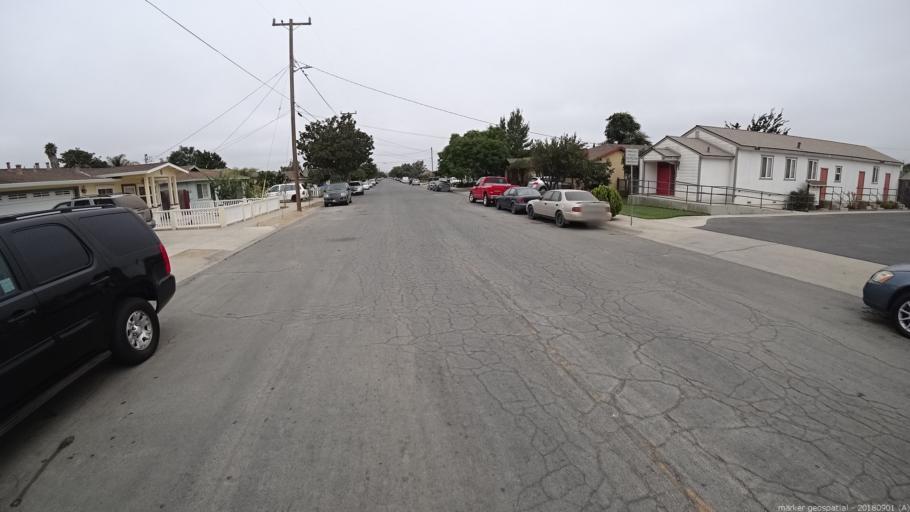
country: US
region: California
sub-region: Monterey County
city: Greenfield
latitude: 36.3168
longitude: -121.2430
